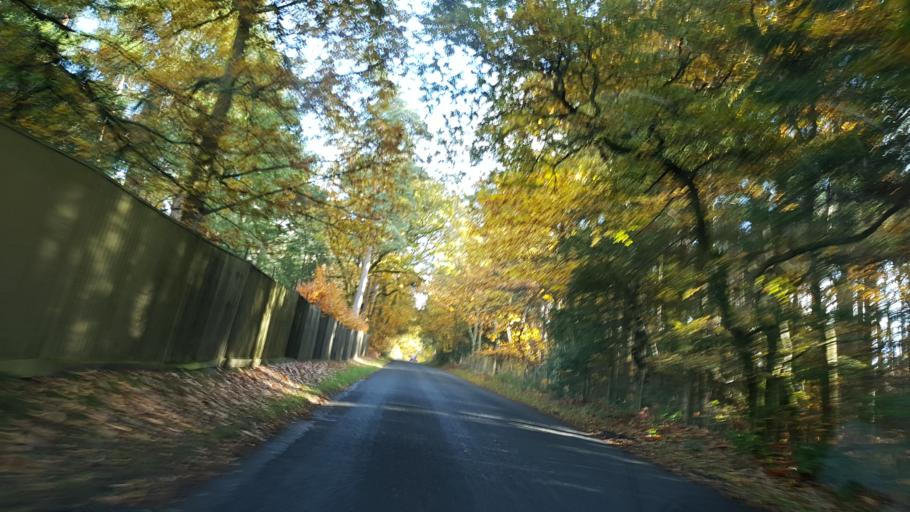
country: GB
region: England
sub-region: Surrey
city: Churt
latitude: 51.1463
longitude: -0.7437
